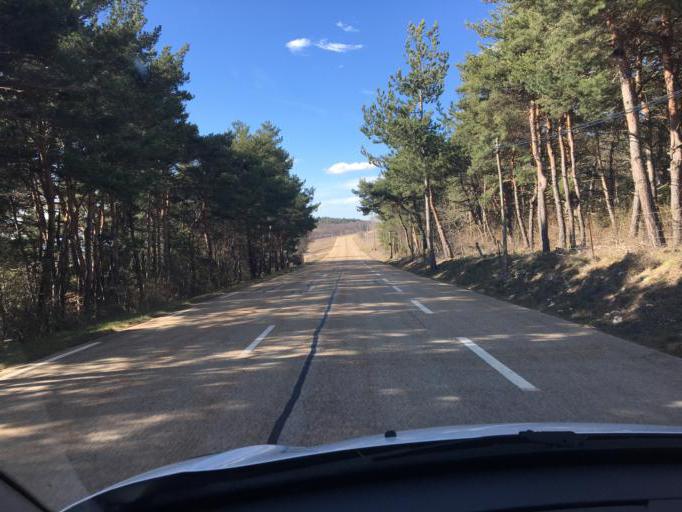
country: FR
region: Provence-Alpes-Cote d'Azur
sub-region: Departement du Vaucluse
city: Sault
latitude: 44.0210
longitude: 5.4698
